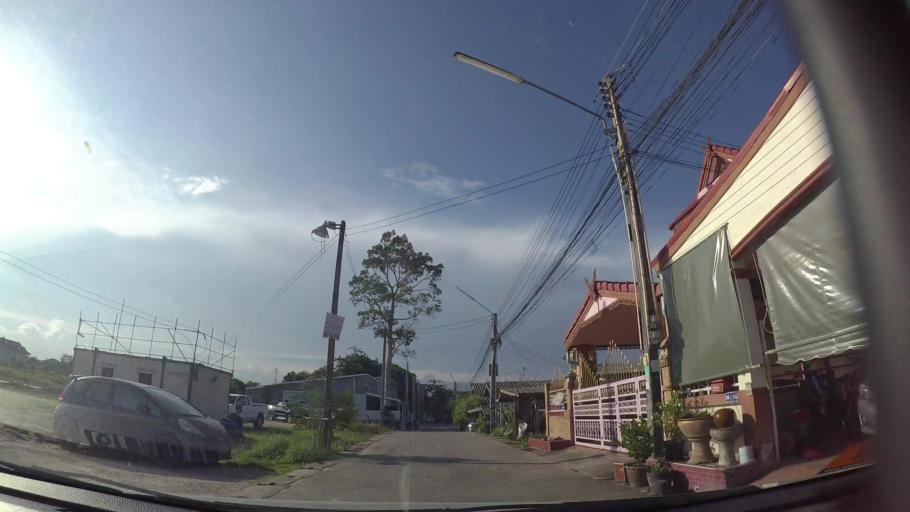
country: TH
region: Rayong
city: Rayong
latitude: 12.6919
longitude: 101.2776
